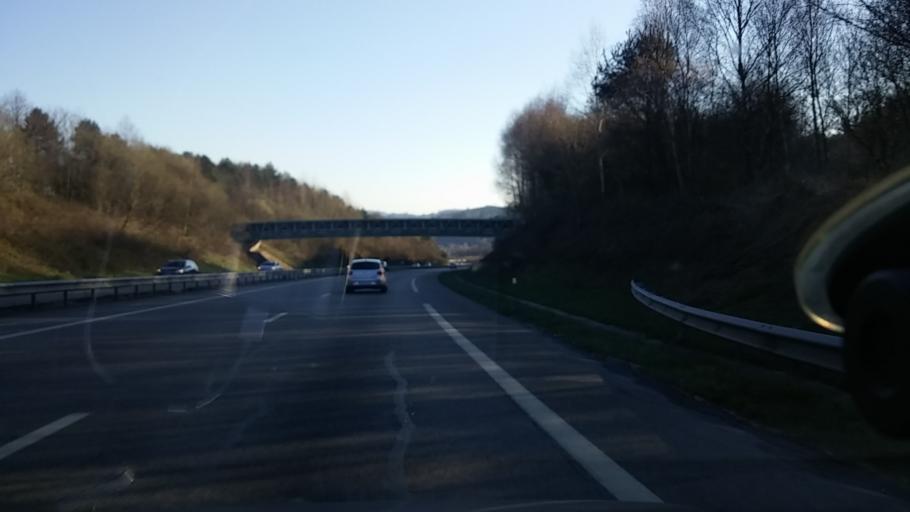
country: FR
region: Limousin
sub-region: Departement de la Haute-Vienne
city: Razes
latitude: 46.0521
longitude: 1.3582
